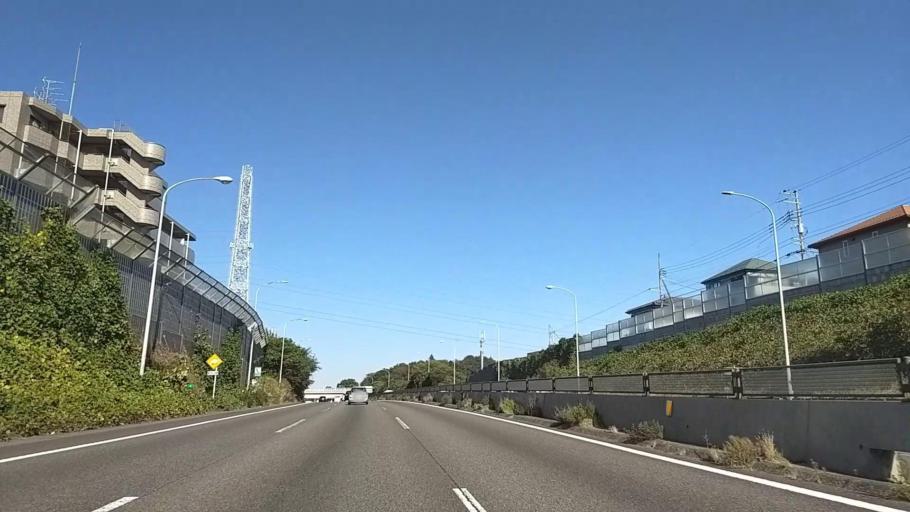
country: JP
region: Kanagawa
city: Minami-rinkan
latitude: 35.4705
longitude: 139.5327
